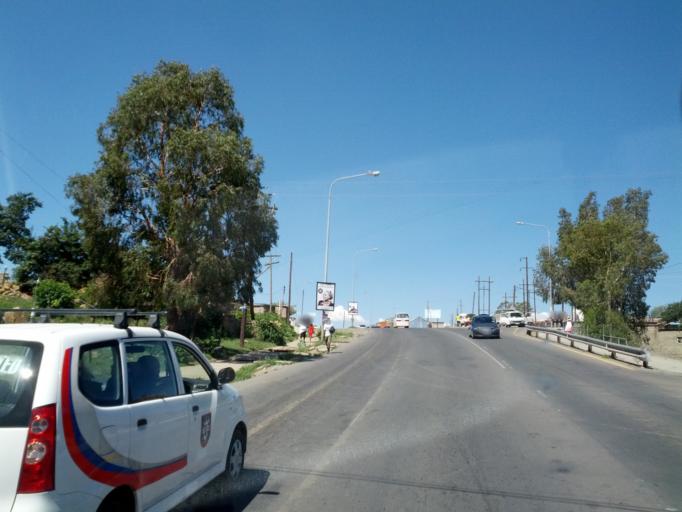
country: LS
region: Maseru
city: Maseru
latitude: -29.3390
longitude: 27.4692
